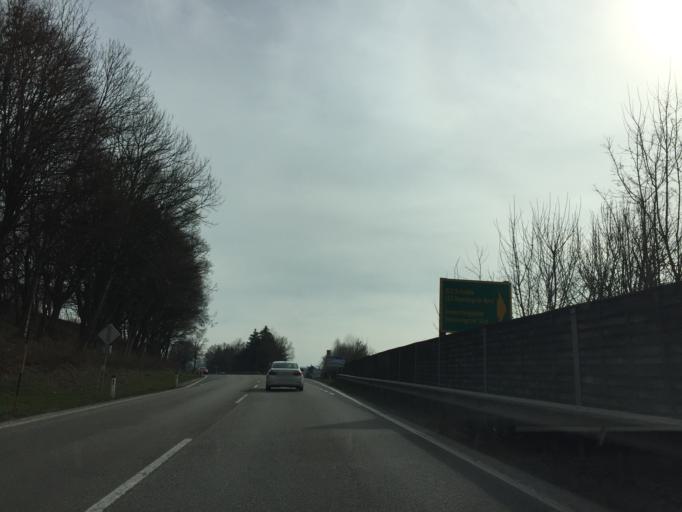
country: AT
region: Upper Austria
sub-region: Politischer Bezirk Ried im Innkreis
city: Ried im Innkreis
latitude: 48.2198
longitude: 13.4921
